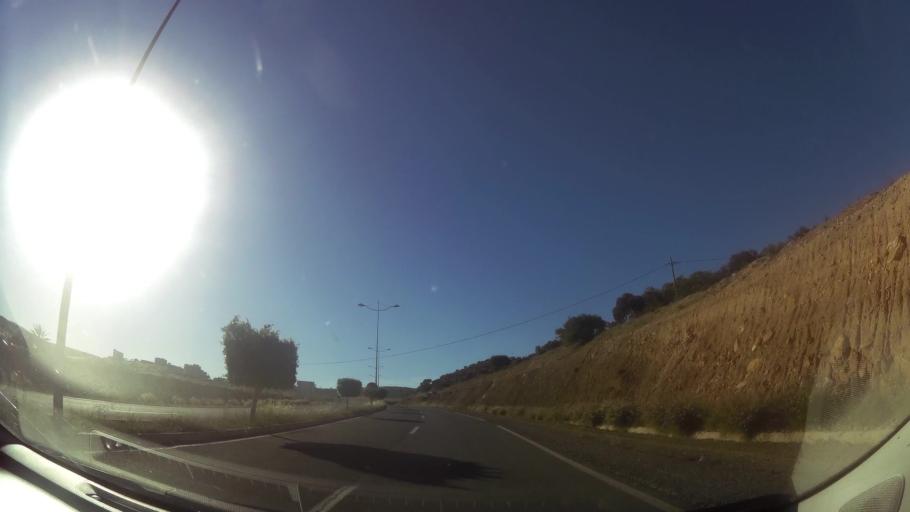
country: MA
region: Oriental
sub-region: Berkane-Taourirt
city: Madagh
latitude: 35.0518
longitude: -2.2194
